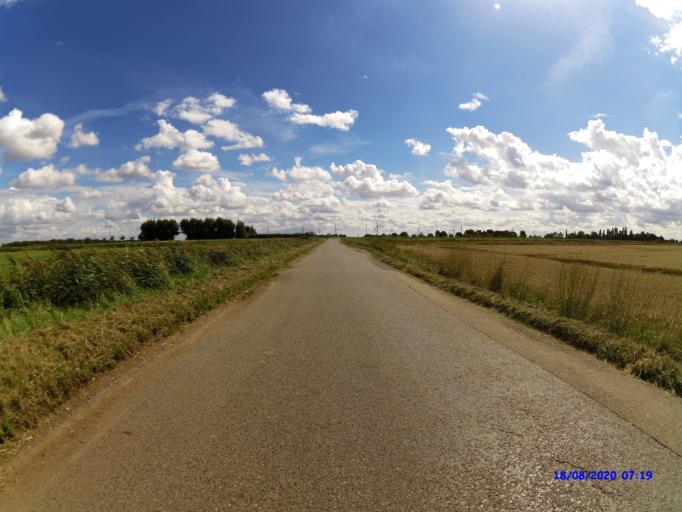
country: GB
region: England
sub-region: Cambridgeshire
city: Whittlesey
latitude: 52.5306
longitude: -0.1029
